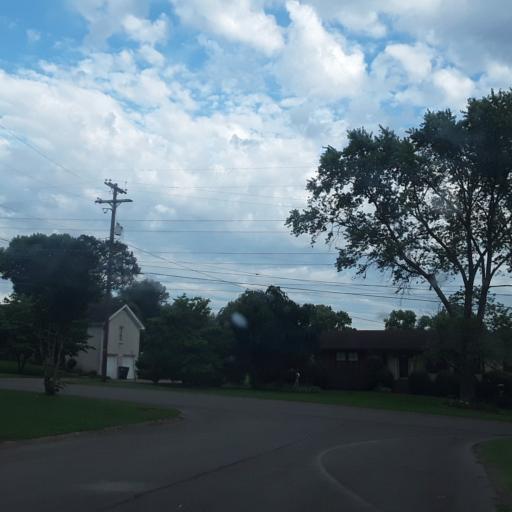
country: US
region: Tennessee
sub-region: Wilson County
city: Green Hill
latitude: 36.1677
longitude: -86.5887
